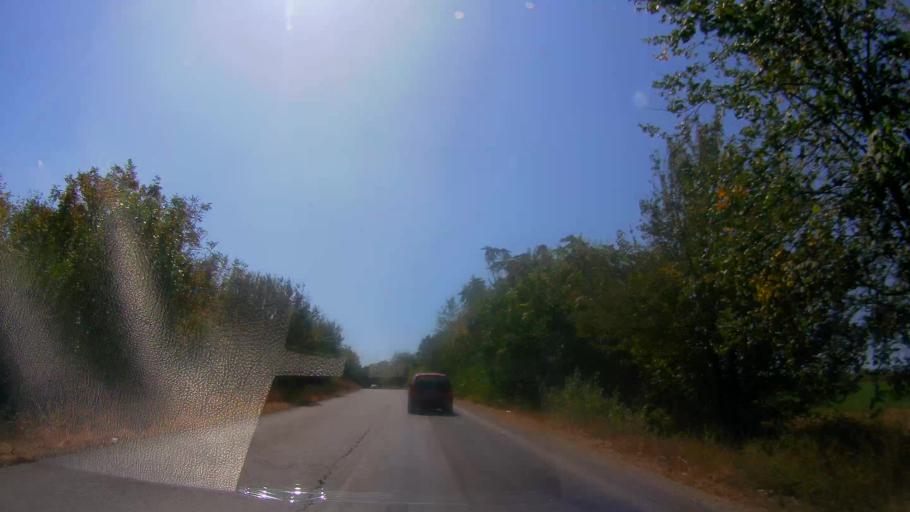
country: BG
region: Veliko Turnovo
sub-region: Obshtina Gorna Oryakhovitsa
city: Purvomaytsi
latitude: 43.2576
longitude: 25.6423
